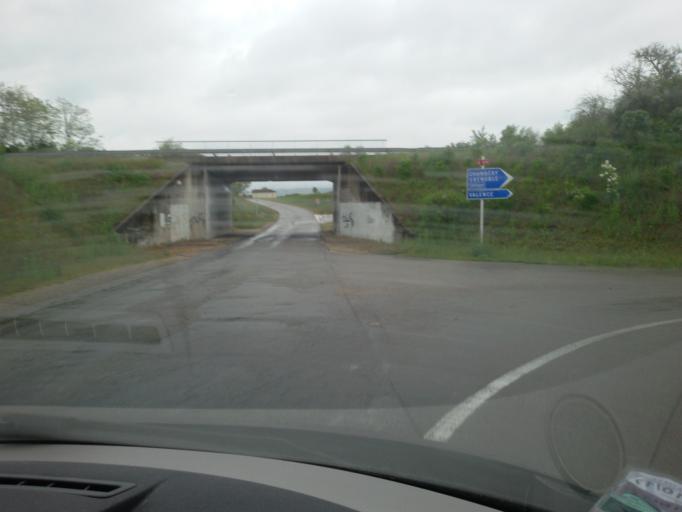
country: FR
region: Rhone-Alpes
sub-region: Departement de la Drome
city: Bourg-de-Peage
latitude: 45.0317
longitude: 5.0792
